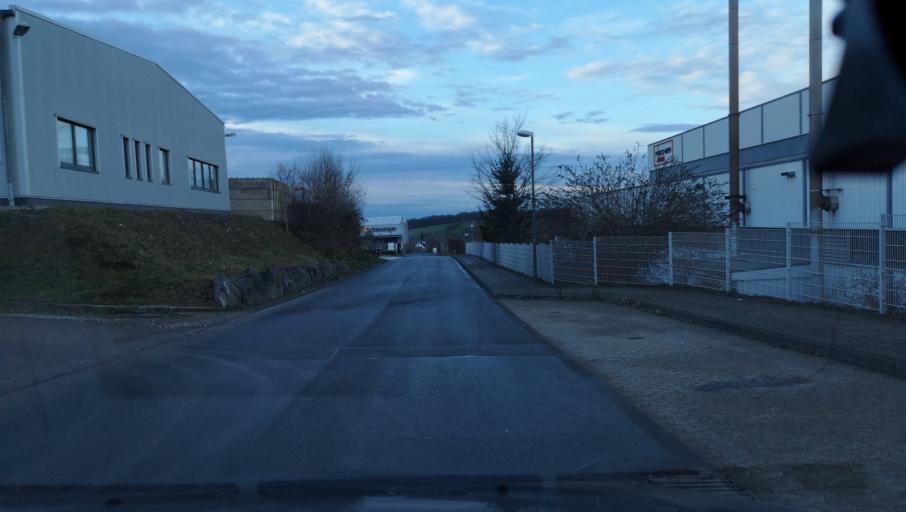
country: DE
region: North Rhine-Westphalia
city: Radevormwald
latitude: 51.2046
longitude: 7.3803
